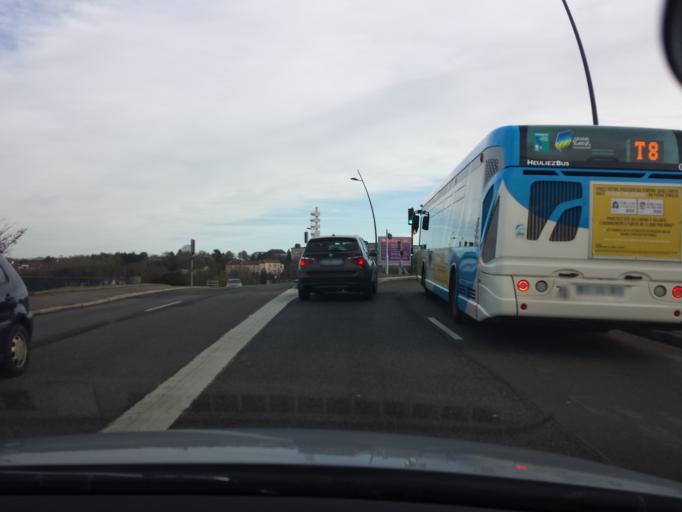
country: FR
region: Haute-Normandie
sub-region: Departement de l'Eure
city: Evreux
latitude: 49.0194
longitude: 1.1539
